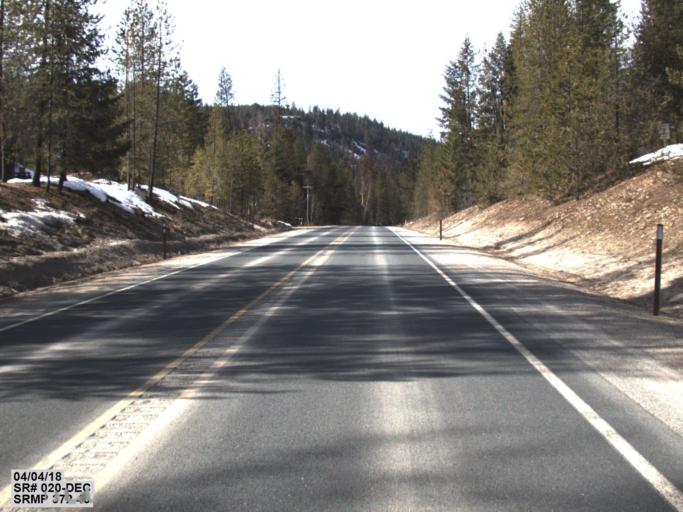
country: US
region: Washington
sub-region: Stevens County
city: Chewelah
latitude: 48.5382
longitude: -117.6041
